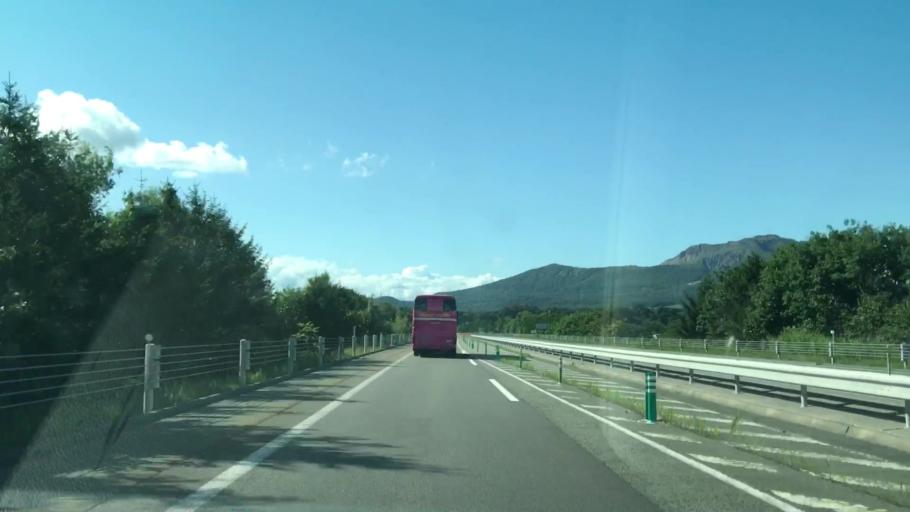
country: JP
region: Hokkaido
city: Date
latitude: 42.4907
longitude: 140.8797
